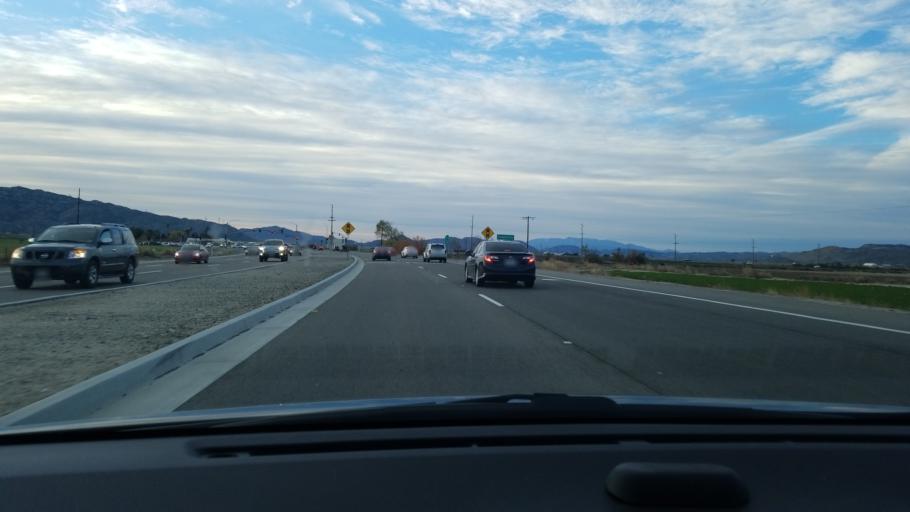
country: US
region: California
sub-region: Riverside County
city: San Jacinto
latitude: 33.8228
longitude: -117.0005
